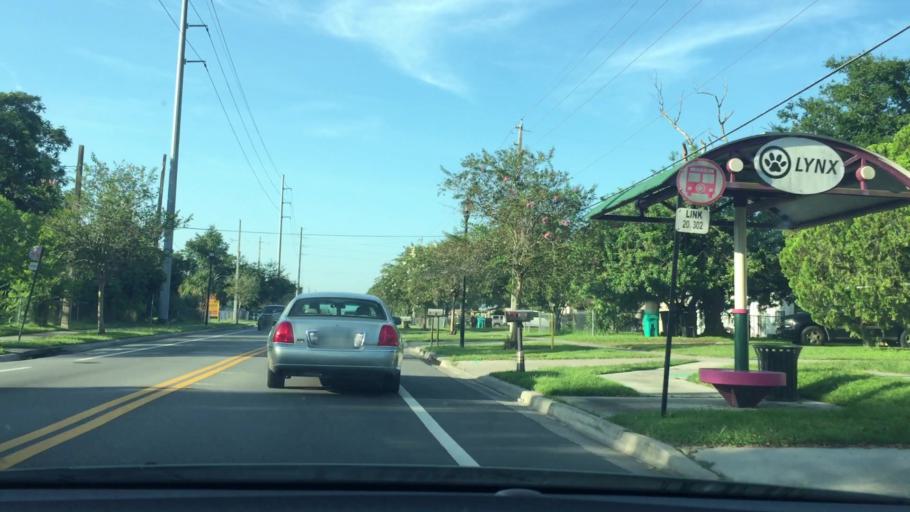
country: US
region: Florida
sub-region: Orange County
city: Pine Hills
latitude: 28.5586
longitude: -81.4305
